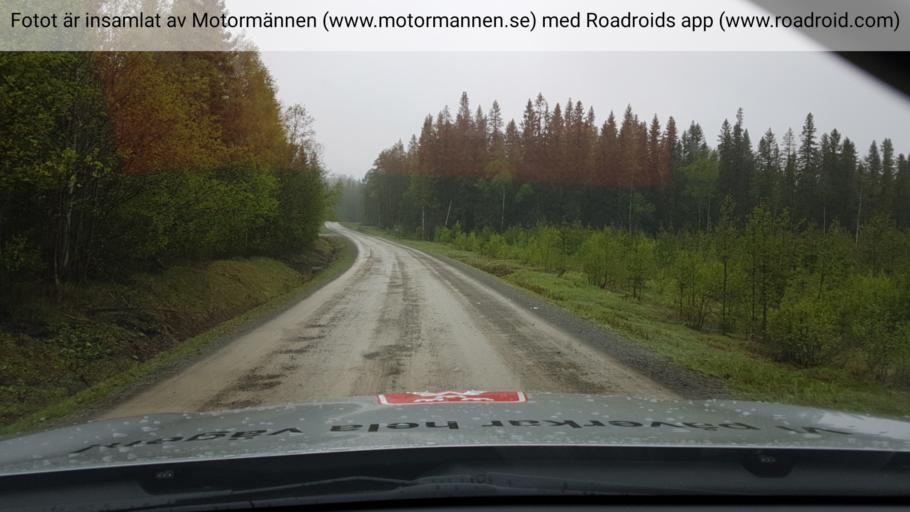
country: SE
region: Jaemtland
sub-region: Bergs Kommun
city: Hoverberg
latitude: 63.0007
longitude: 14.1414
